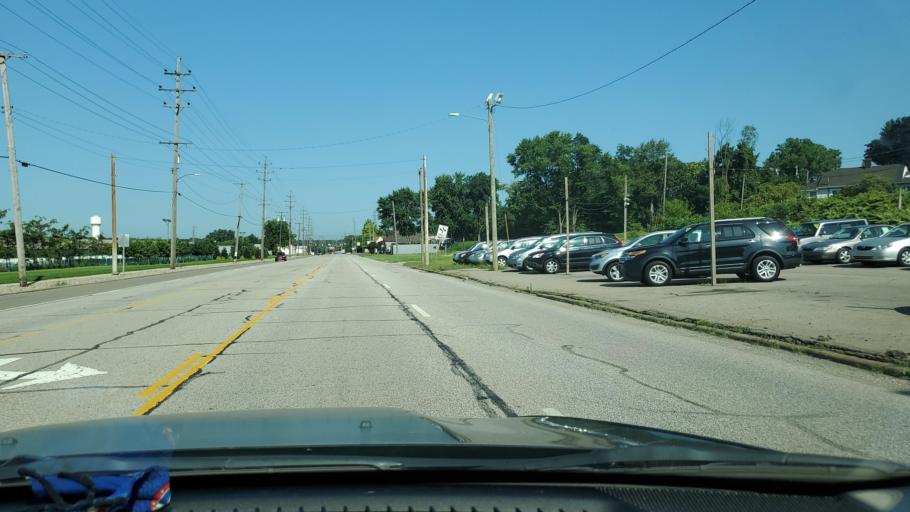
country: US
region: Ohio
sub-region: Trumbull County
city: Girard
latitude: 41.1388
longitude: -80.6892
